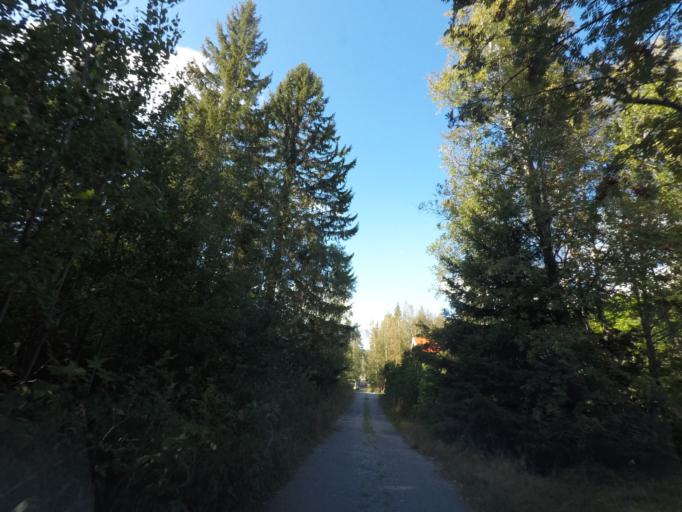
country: SE
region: Vaestmanland
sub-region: Skinnskattebergs Kommun
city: Skinnskatteberg
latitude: 59.8296
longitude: 15.5508
